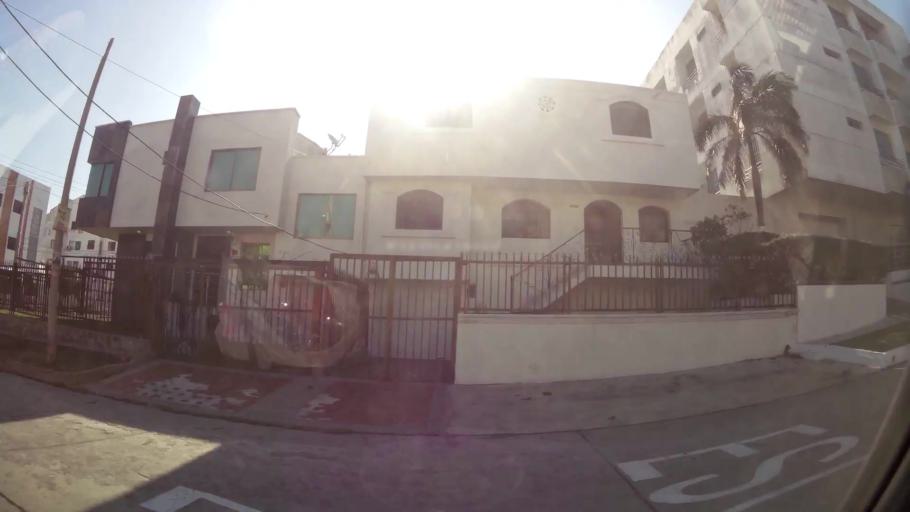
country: CO
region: Atlantico
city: Barranquilla
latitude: 11.0018
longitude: -74.8303
